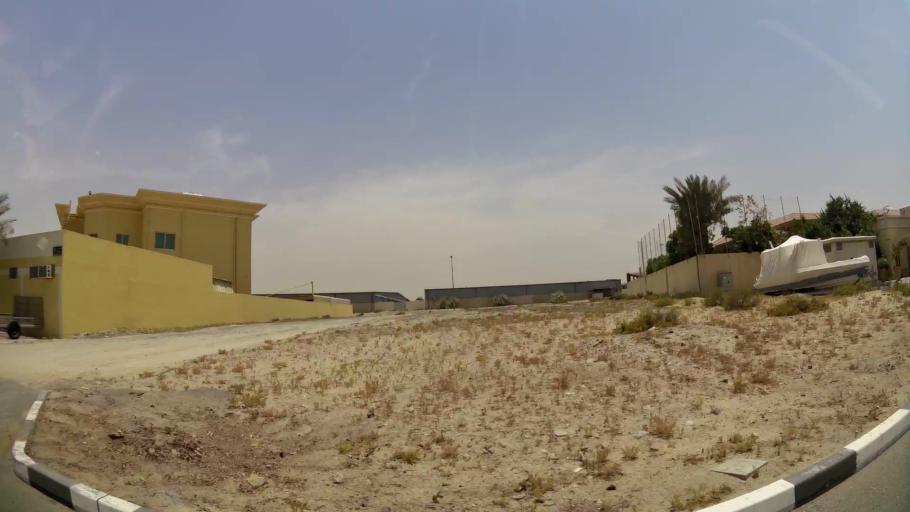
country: AE
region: Ash Shariqah
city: Sharjah
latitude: 25.1924
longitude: 55.3744
